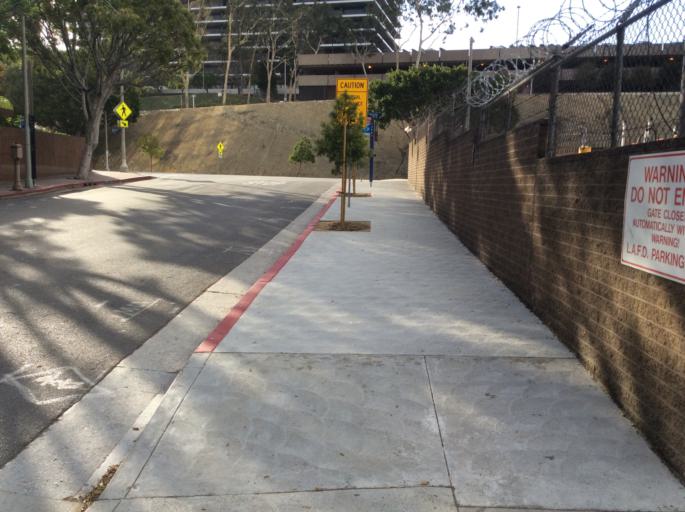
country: US
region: California
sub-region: Los Angeles County
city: Los Angeles
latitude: 34.0586
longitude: -118.2519
